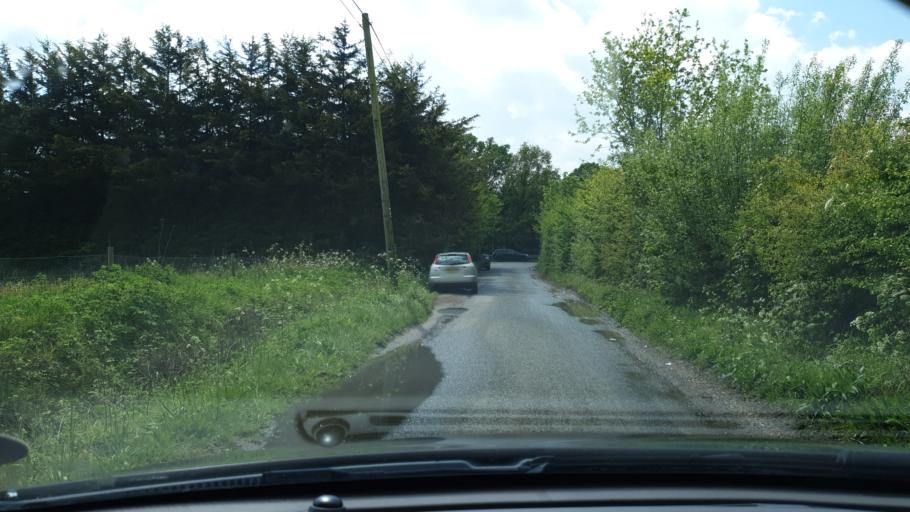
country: GB
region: England
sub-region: Essex
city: Great Bentley
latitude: 51.8709
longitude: 1.0621
